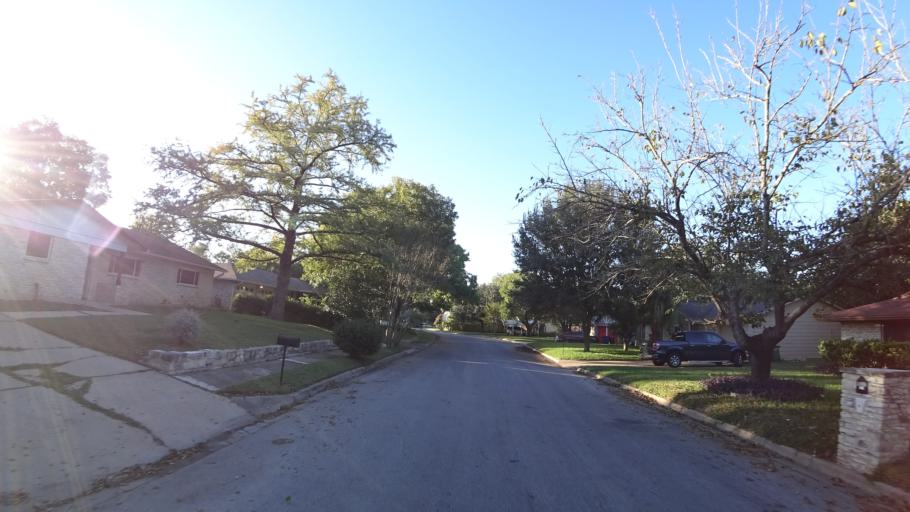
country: US
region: Texas
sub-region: Travis County
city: Austin
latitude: 30.3013
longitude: -97.6803
